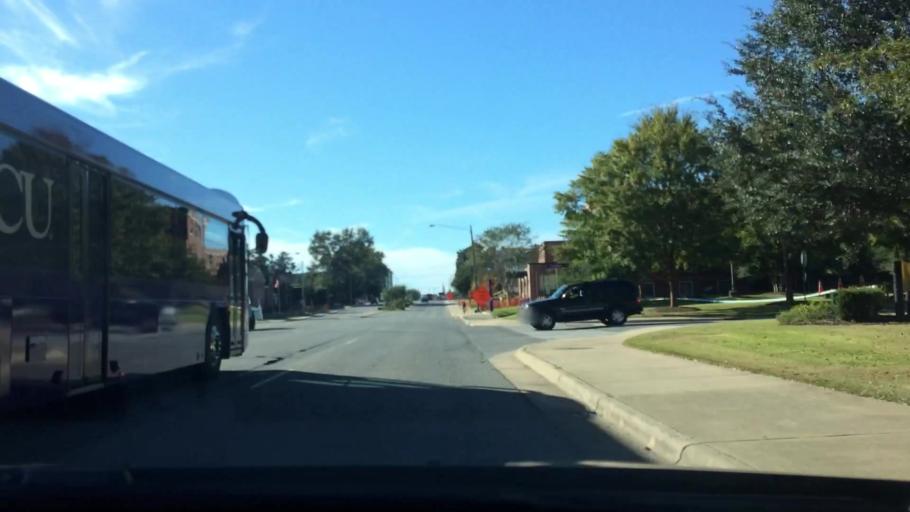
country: US
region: North Carolina
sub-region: Pitt County
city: Greenville
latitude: 35.6046
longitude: -77.3657
